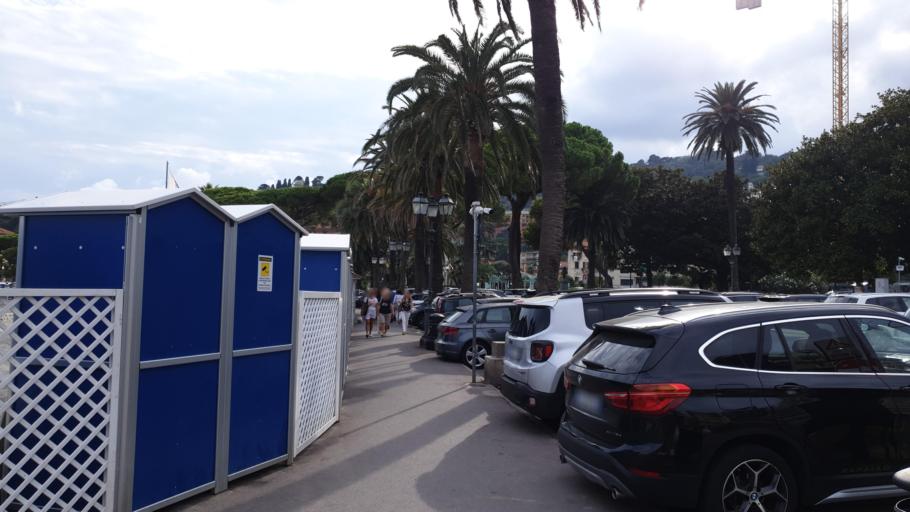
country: IT
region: Liguria
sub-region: Provincia di Genova
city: Rapallo
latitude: 44.3480
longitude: 9.2295
